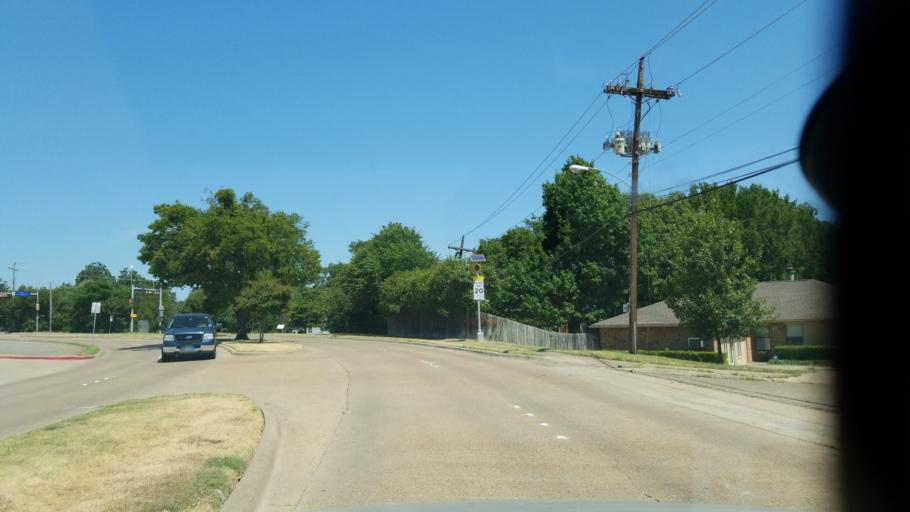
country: US
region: Texas
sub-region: Dallas County
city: Duncanville
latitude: 32.6500
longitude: -96.9000
